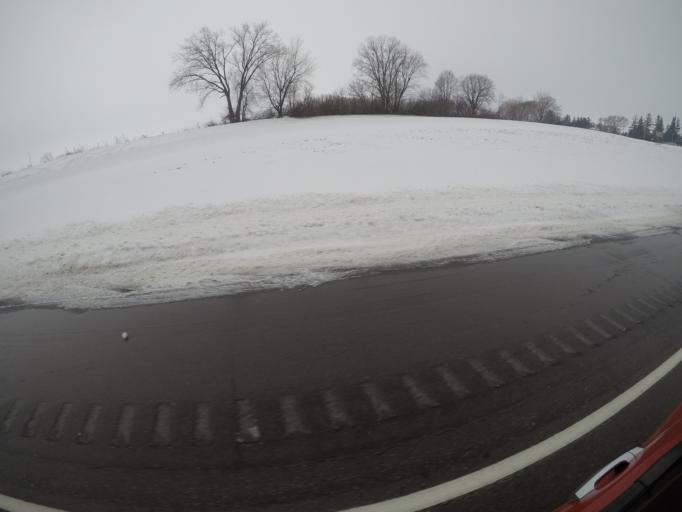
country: US
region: Minnesota
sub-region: Goodhue County
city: Zumbrota
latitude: 44.2917
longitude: -92.6840
